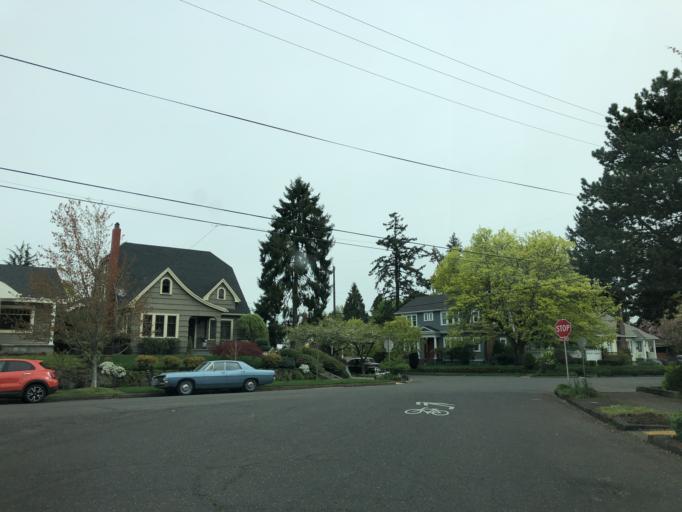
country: US
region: Oregon
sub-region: Multnomah County
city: Portland
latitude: 45.5529
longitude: -122.6332
